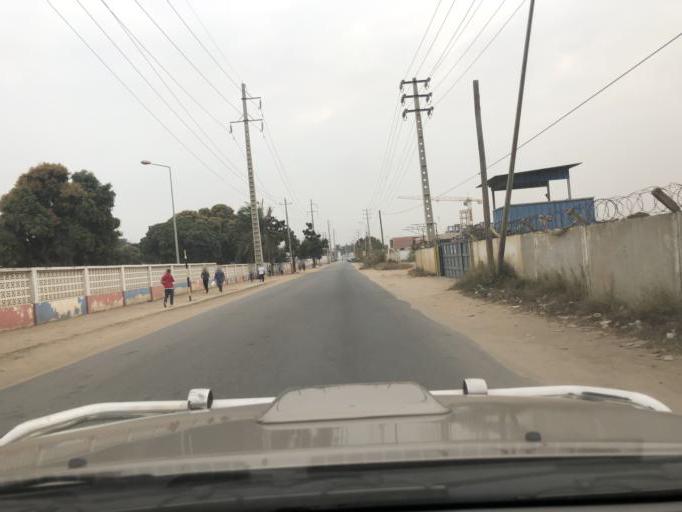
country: AO
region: Luanda
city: Luanda
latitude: -8.8912
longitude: 13.1890
